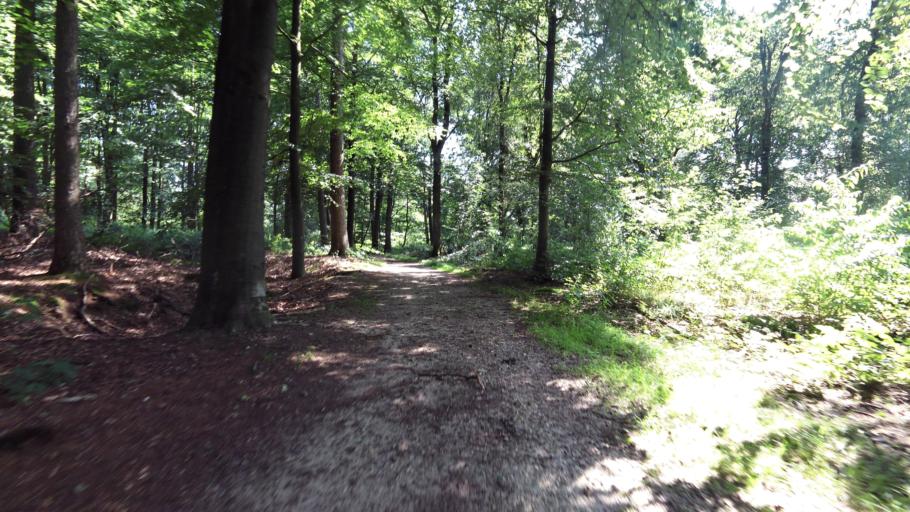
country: NL
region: Gelderland
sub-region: Gemeente Renkum
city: Oosterbeek
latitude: 51.9985
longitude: 5.8456
